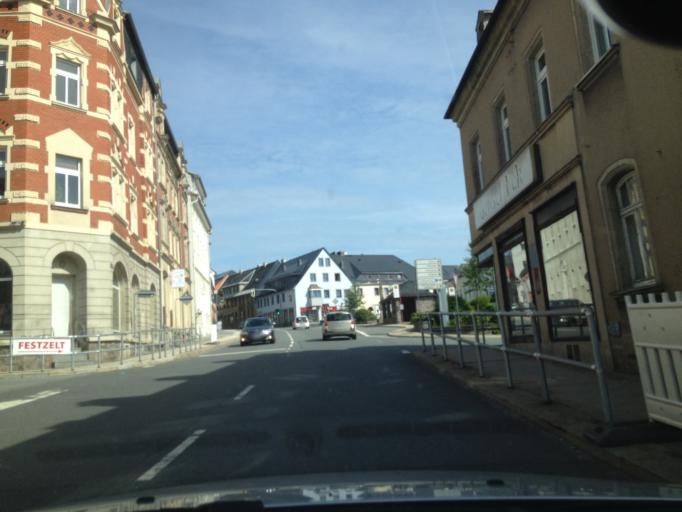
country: DE
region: Saxony
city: Thum
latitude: 50.6703
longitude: 12.9514
